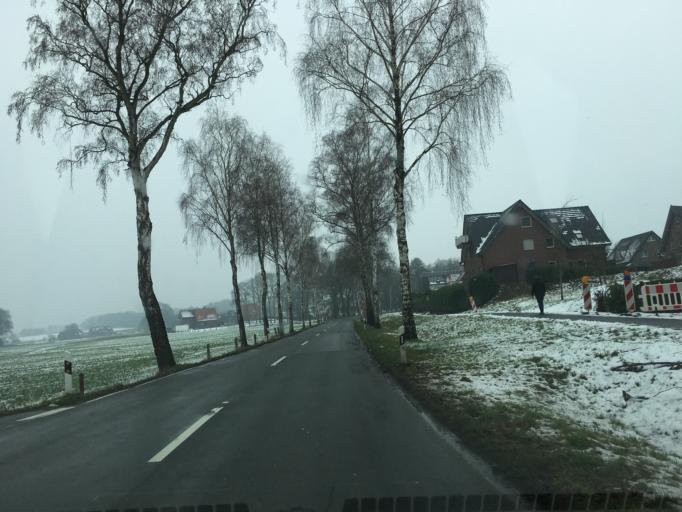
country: DE
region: North Rhine-Westphalia
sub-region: Regierungsbezirk Munster
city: Klein Reken
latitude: 51.7841
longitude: 7.0371
